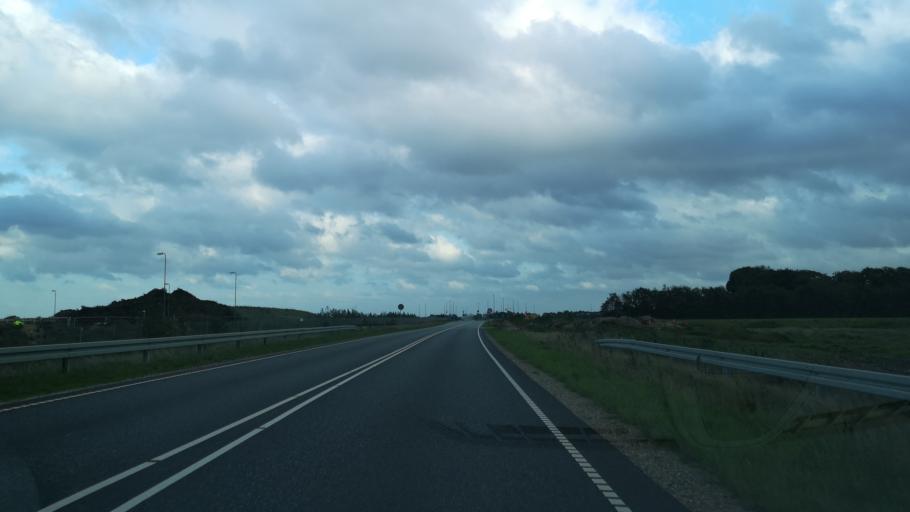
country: DK
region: Central Jutland
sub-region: Herning Kommune
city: Snejbjerg
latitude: 56.1541
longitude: 8.8876
